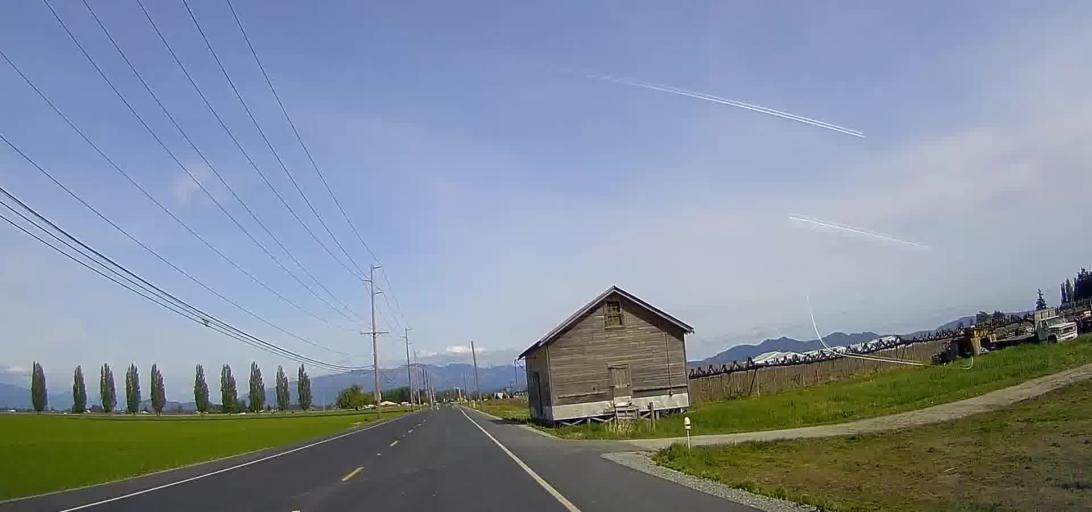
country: US
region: Washington
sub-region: Skagit County
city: Mount Vernon
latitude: 48.4207
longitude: -122.4502
